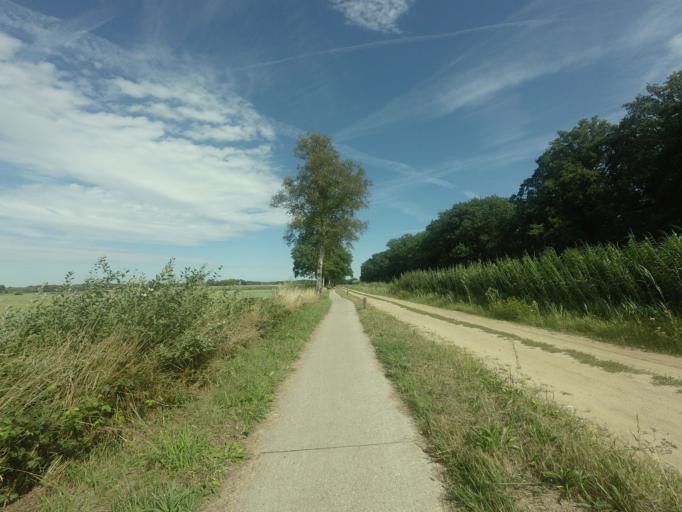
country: NL
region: Overijssel
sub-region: Gemeente Raalte
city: Raalte
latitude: 52.4169
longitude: 6.3186
